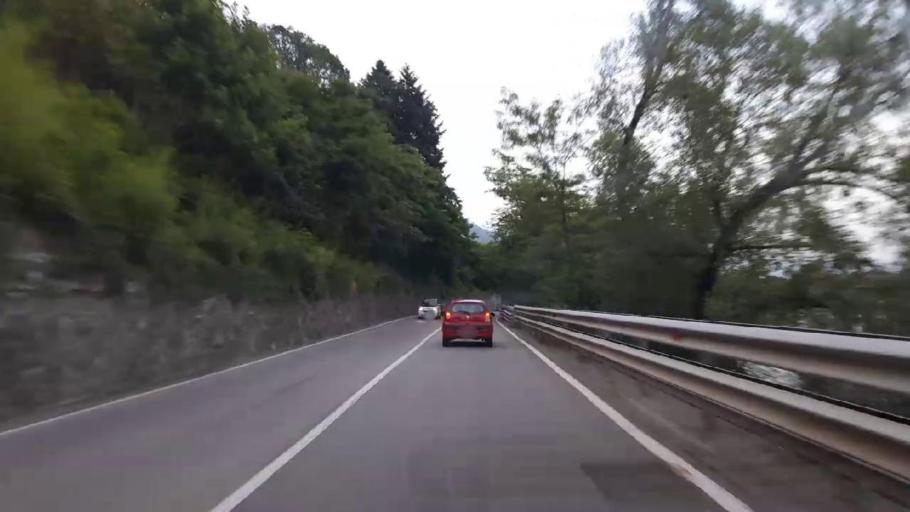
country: IT
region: Piedmont
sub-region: Provincia di Novara
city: Massino Visconti
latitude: 45.8115
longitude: 8.5437
